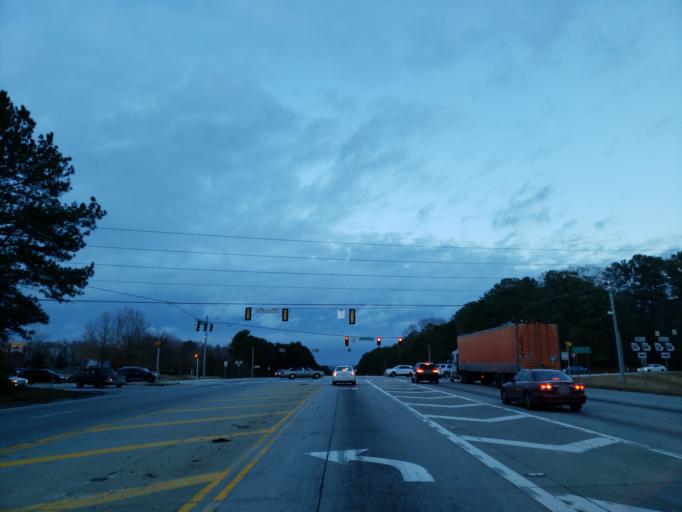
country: US
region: Georgia
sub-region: Fulton County
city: Union City
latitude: 33.6987
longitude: -84.5769
